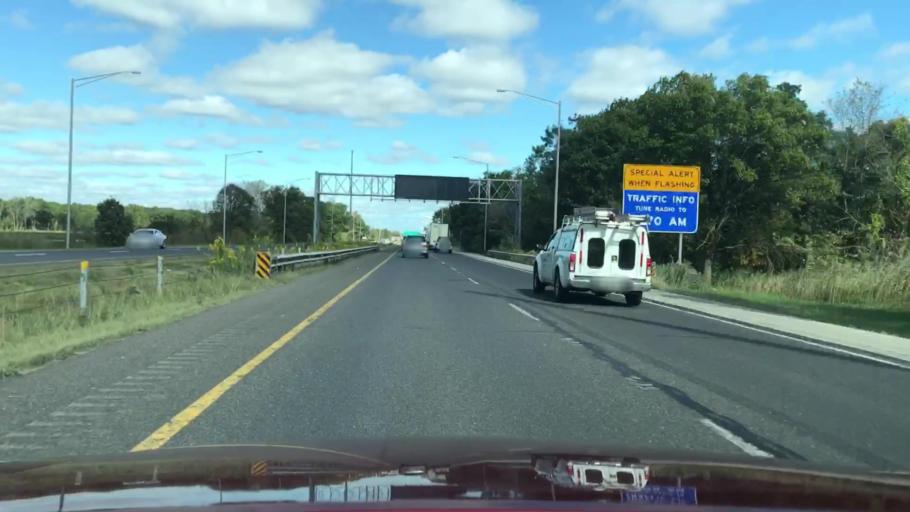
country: US
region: Illinois
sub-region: Cook County
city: Glenwood
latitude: 41.5576
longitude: -87.5835
